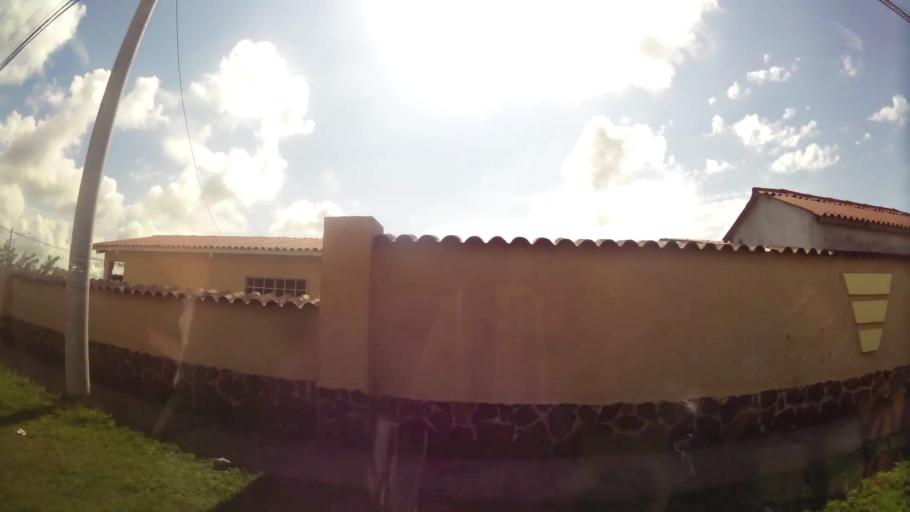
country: PA
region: Panama
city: Nuevo Arraijan
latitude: 8.9041
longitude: -79.7439
